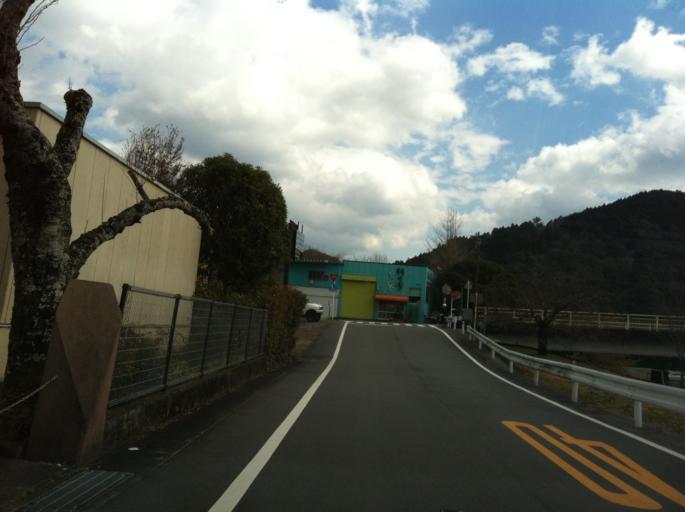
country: JP
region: Shizuoka
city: Kanaya
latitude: 34.9376
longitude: 138.0756
